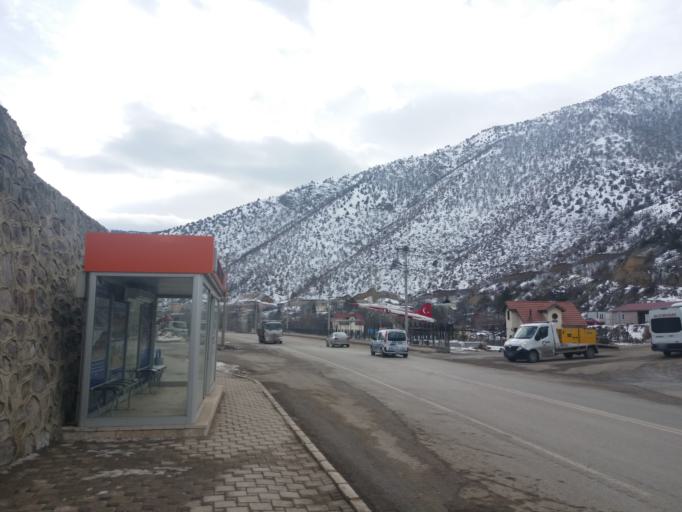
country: TR
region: Gumushane
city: Gumushkhane
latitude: 40.4404
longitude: 39.5039
